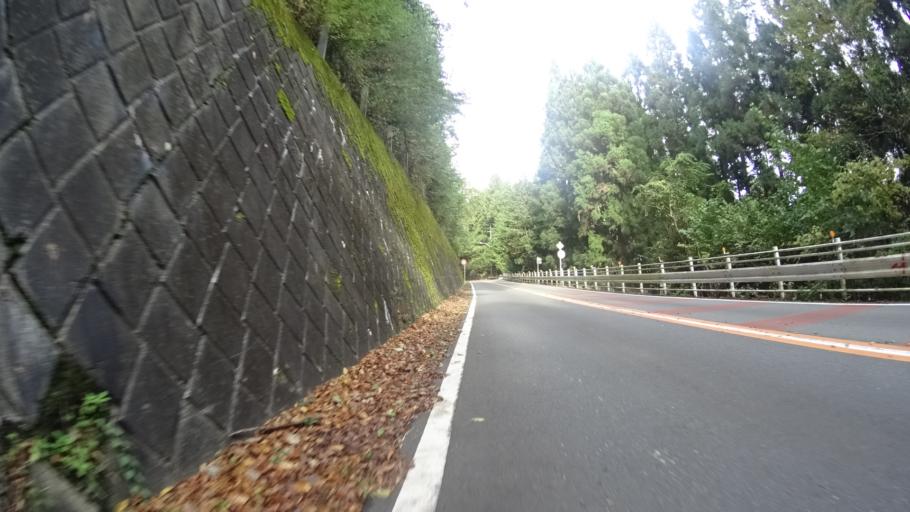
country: JP
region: Yamanashi
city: Uenohara
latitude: 35.6999
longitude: 139.1032
